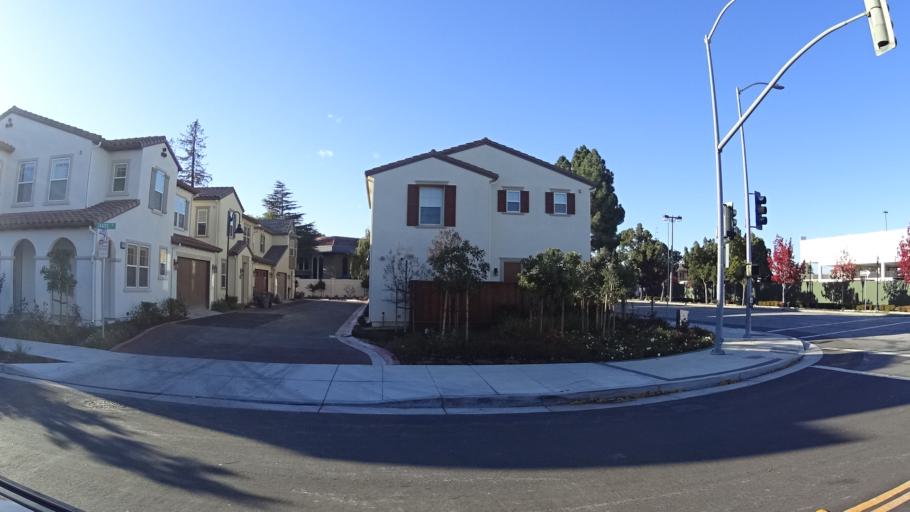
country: US
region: California
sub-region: Santa Clara County
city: Sunnyvale
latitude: 37.3729
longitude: -122.0338
